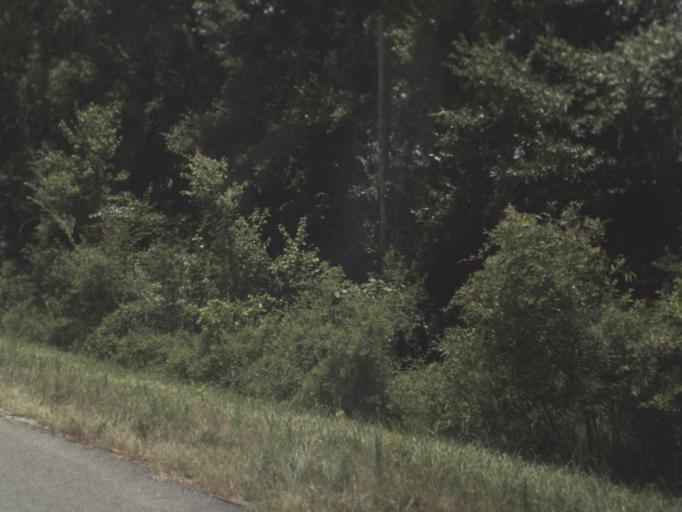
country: US
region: Florida
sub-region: Taylor County
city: Perry
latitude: 30.1190
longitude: -83.7298
